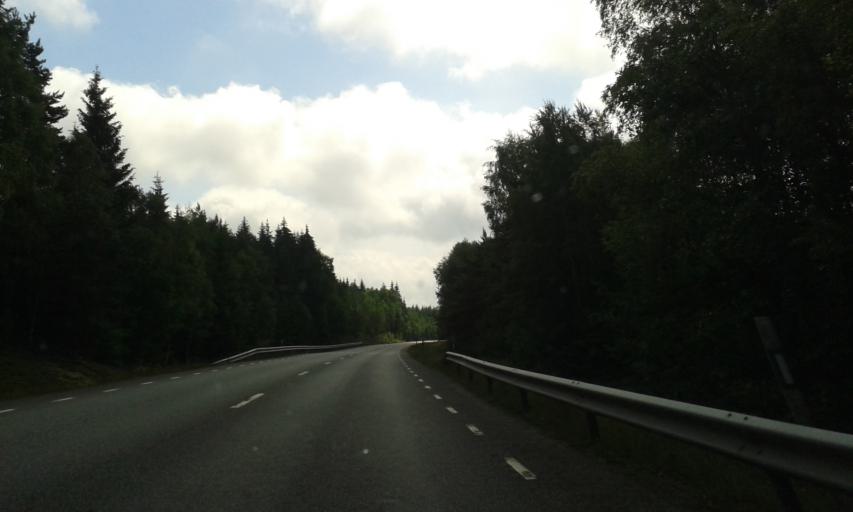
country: SE
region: Vaestra Goetaland
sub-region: Tranemo Kommun
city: Langhem
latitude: 57.5998
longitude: 13.1739
